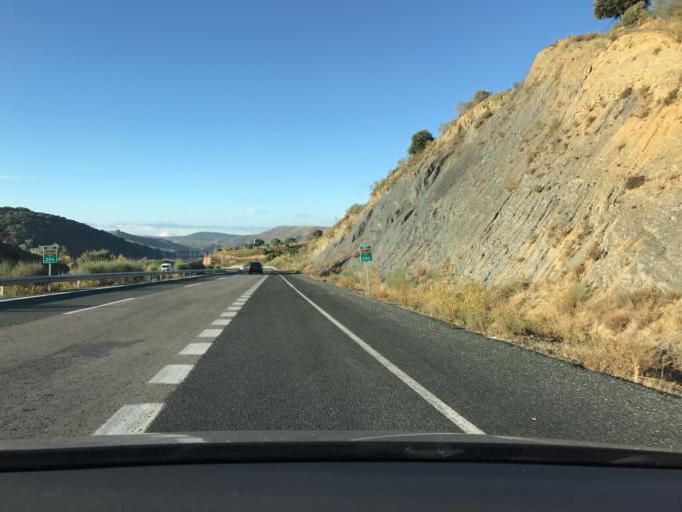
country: ES
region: Andalusia
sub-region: Provincia de Granada
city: Huetor Santillan
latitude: 37.2332
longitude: -3.4992
